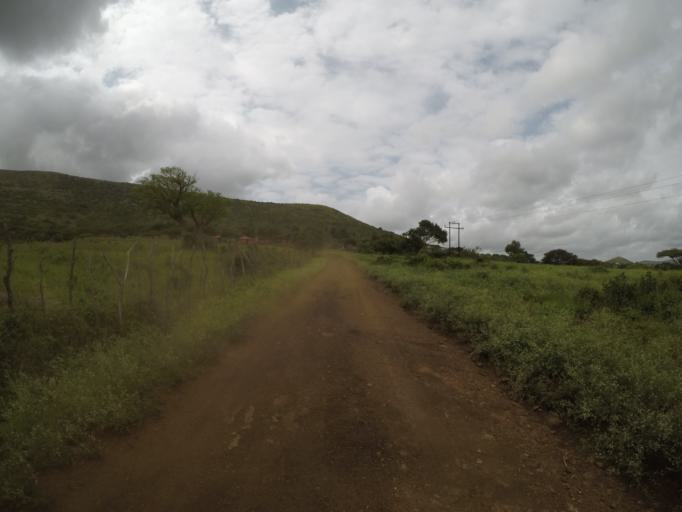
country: ZA
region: KwaZulu-Natal
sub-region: uThungulu District Municipality
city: Empangeni
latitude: -28.6016
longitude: 31.8945
